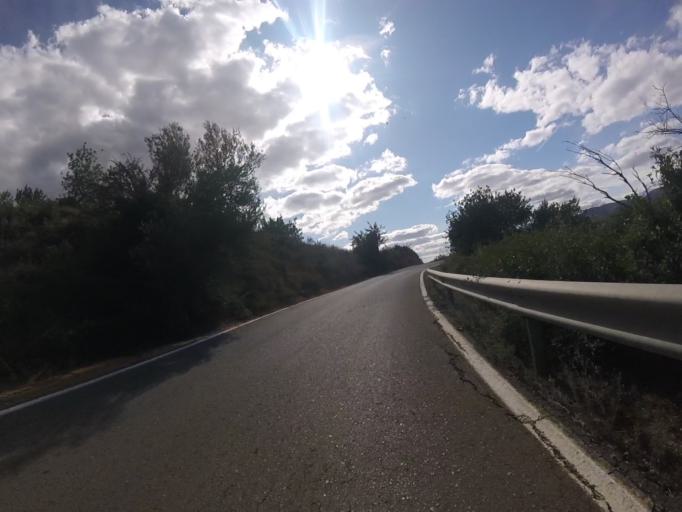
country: ES
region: Valencia
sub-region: Provincia de Castello
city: Cuevas de Vinroma
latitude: 40.3667
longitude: 0.1215
